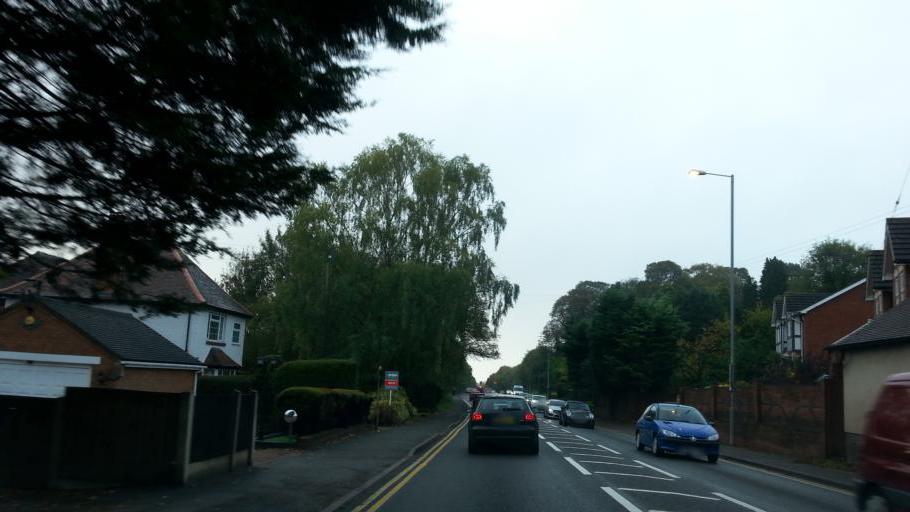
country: GB
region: England
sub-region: Worcestershire
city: Bromsgrove
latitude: 52.3504
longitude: -2.0479
